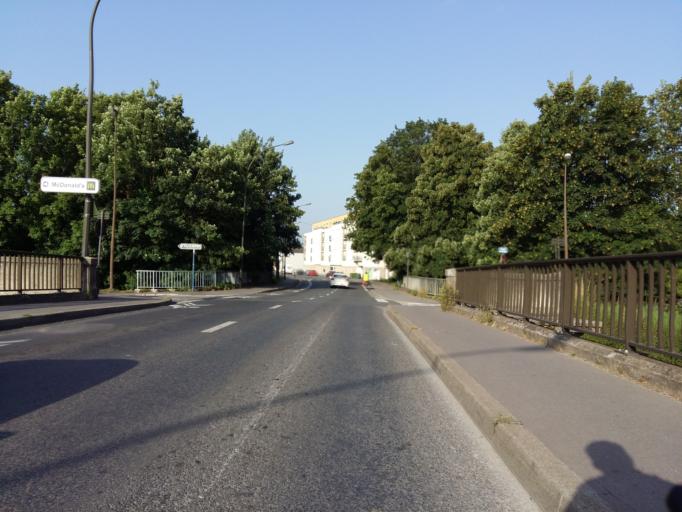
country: FR
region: Picardie
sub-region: Departement de la Somme
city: Amiens
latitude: 49.9034
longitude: 2.2867
